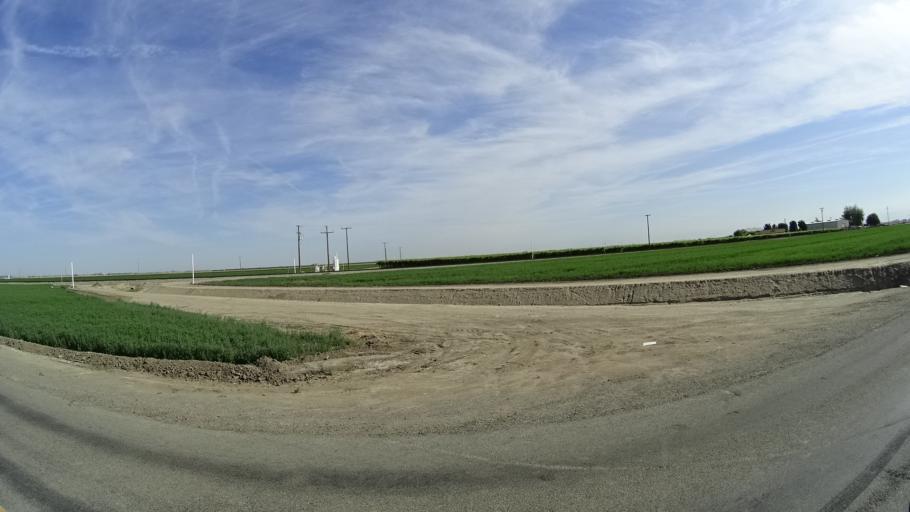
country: US
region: California
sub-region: Tulare County
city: Goshen
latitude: 36.3492
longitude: -119.4842
